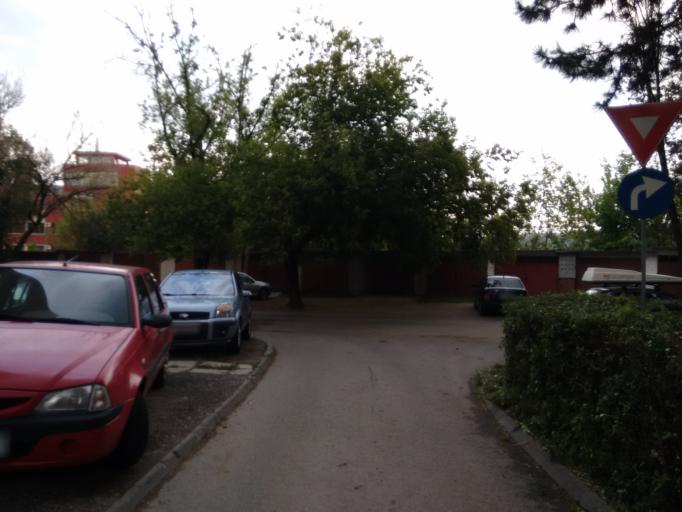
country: RO
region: Cluj
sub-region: Municipiul Cluj-Napoca
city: Cluj-Napoca
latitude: 46.7640
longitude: 23.6235
